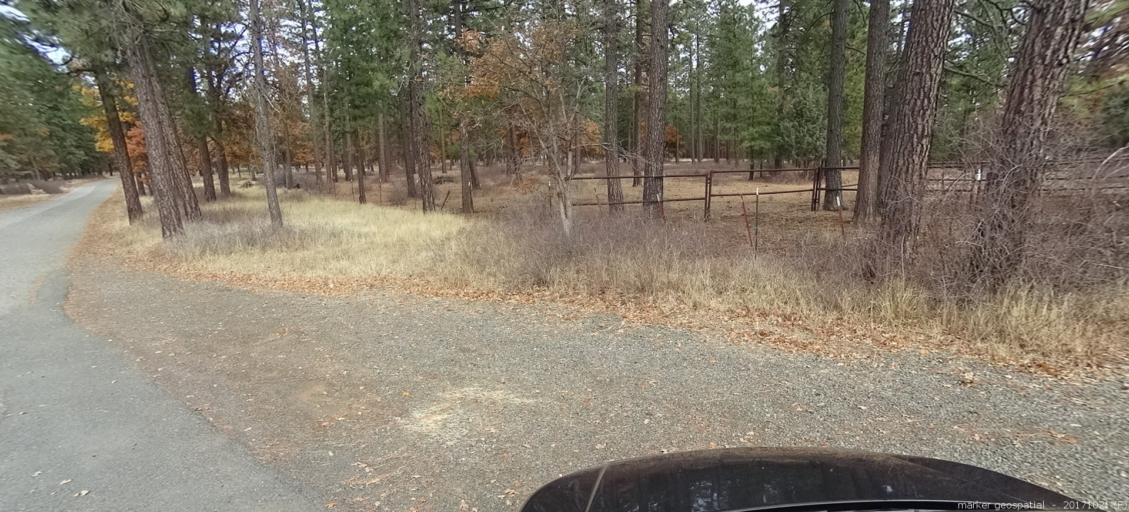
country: US
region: California
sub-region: Shasta County
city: Burney
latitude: 40.9248
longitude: -121.6589
